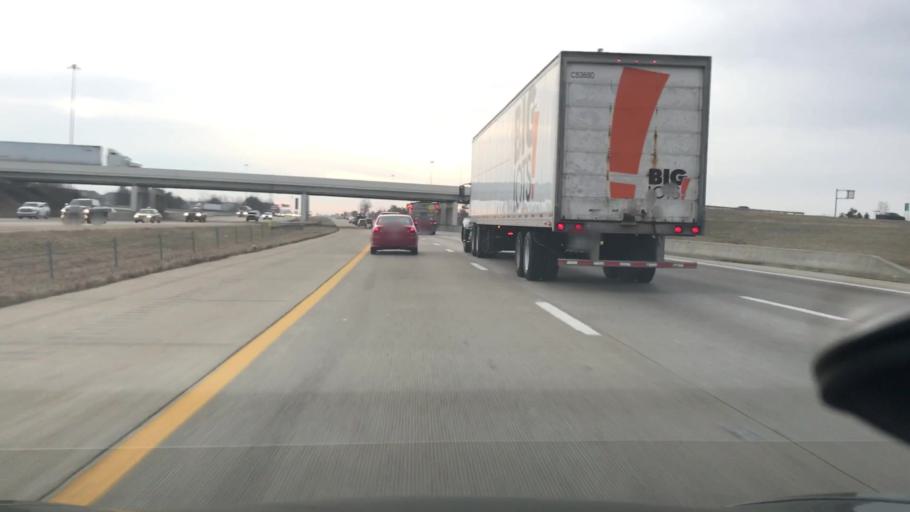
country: US
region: Ohio
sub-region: Franklin County
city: Lincoln Village
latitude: 39.9244
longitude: -83.1212
